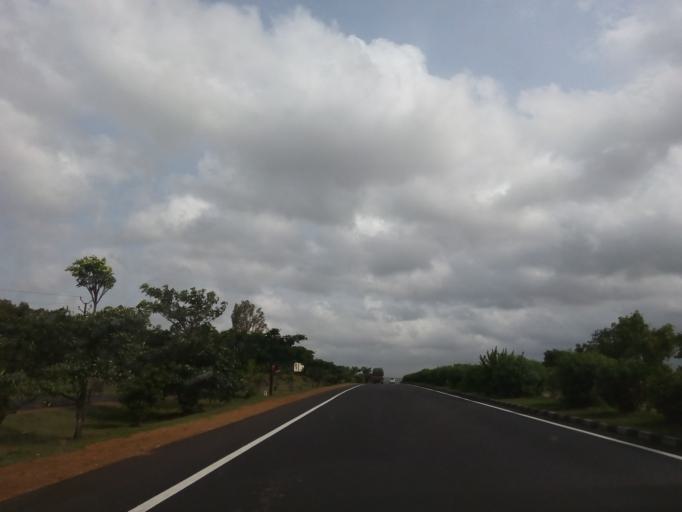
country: IN
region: Karnataka
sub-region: Belgaum
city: Hukeri
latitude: 16.1207
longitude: 74.5175
